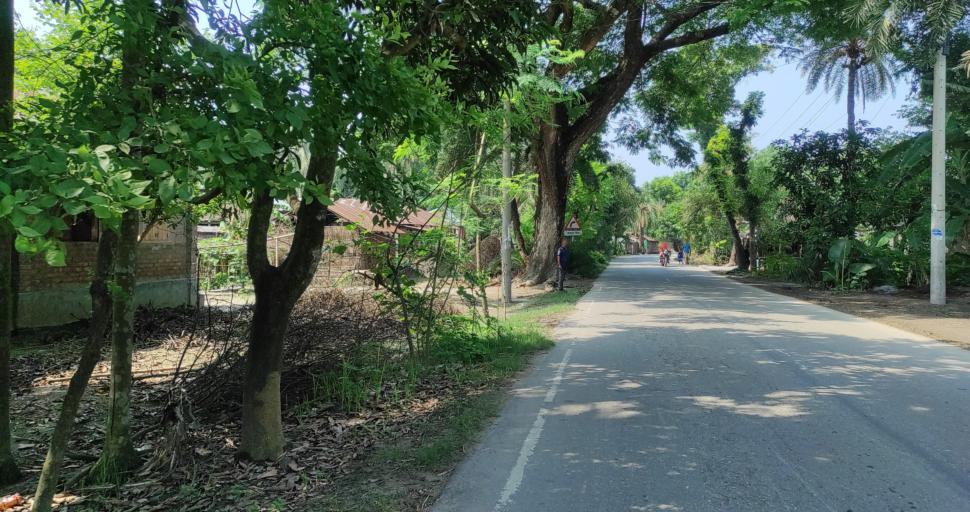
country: BD
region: Rajshahi
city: Ishurdi
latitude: 24.2587
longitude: 89.0486
